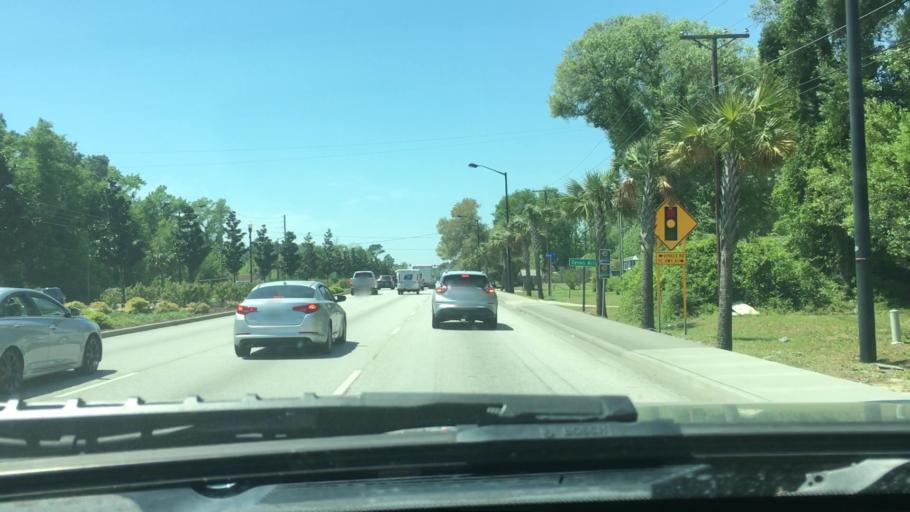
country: US
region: South Carolina
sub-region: Charleston County
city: Isle of Palms
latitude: 32.8610
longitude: -79.7924
